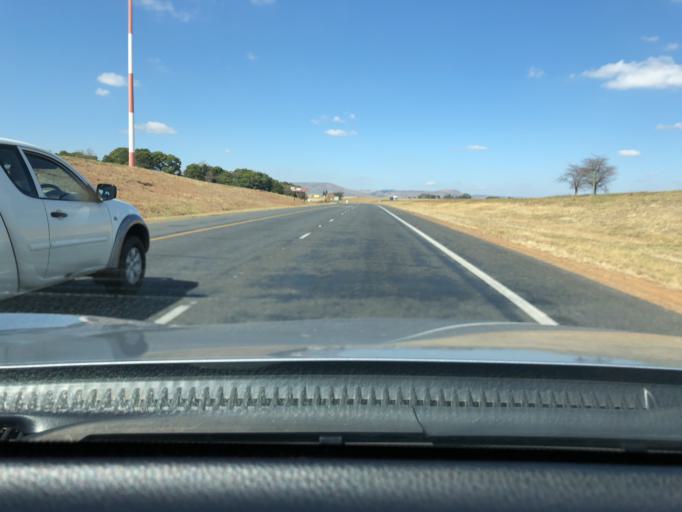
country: ZA
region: KwaZulu-Natal
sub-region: uThukela District Municipality
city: Estcourt
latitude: -29.0161
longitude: 29.8199
